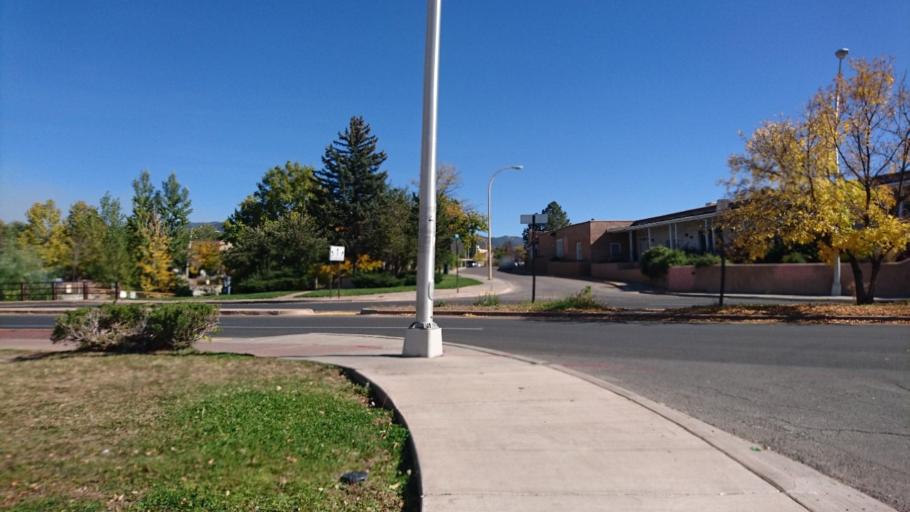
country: US
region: New Mexico
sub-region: Santa Fe County
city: Santa Fe
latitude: 35.6862
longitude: -105.9433
